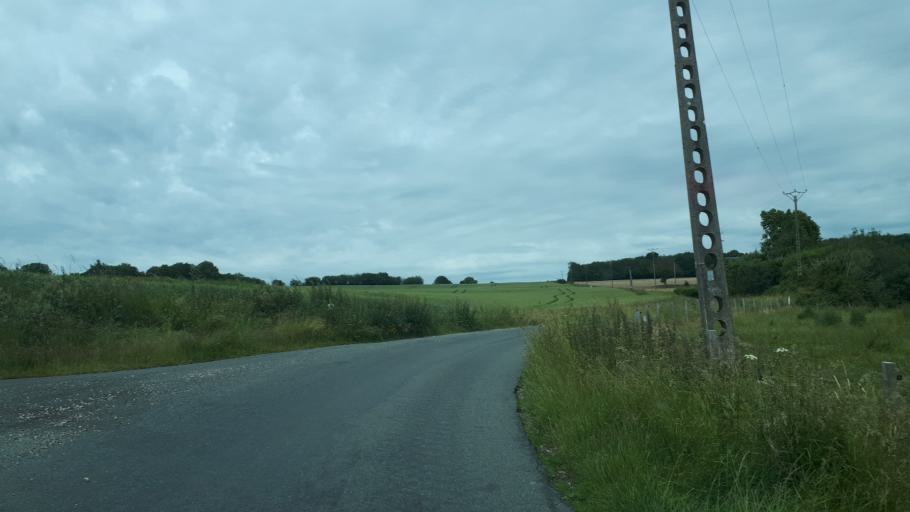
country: FR
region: Centre
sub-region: Departement du Cher
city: Blancafort
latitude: 47.4179
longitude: 2.6163
